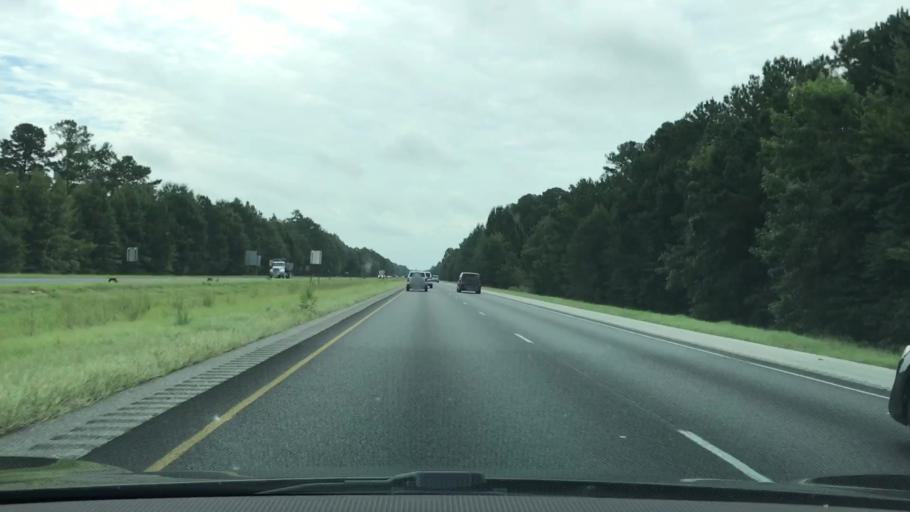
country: US
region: Alabama
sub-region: Montgomery County
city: Pike Road
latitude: 32.3746
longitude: -86.0319
